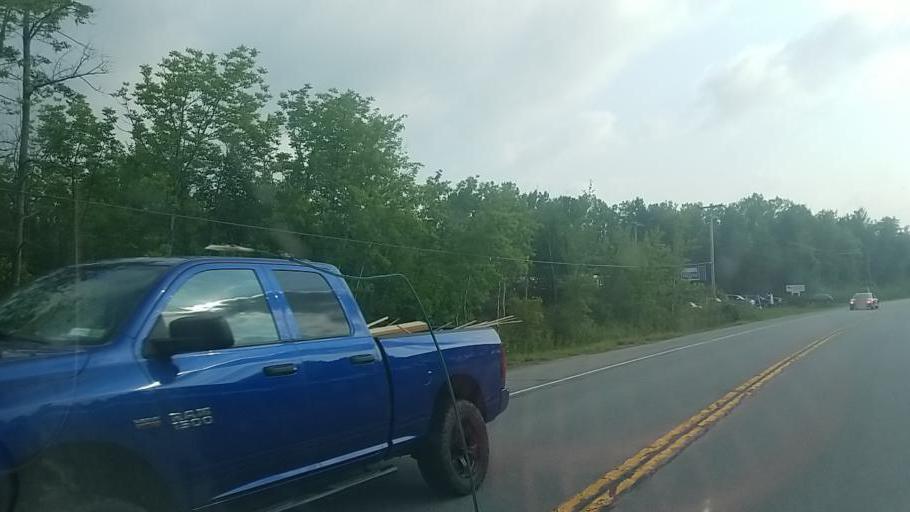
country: US
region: New York
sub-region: Fulton County
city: Johnstown
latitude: 43.0254
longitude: -74.3583
